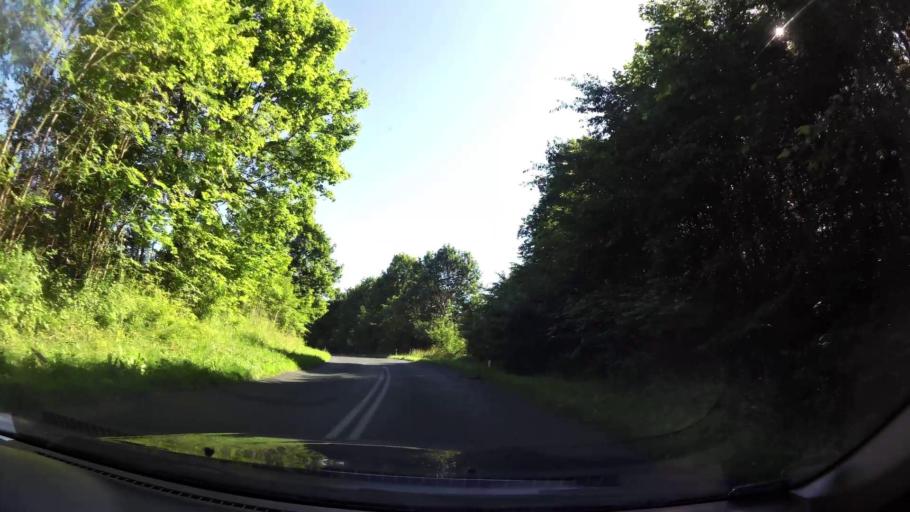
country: PL
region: West Pomeranian Voivodeship
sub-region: Powiat stargardzki
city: Dobrzany
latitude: 53.4178
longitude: 15.4243
